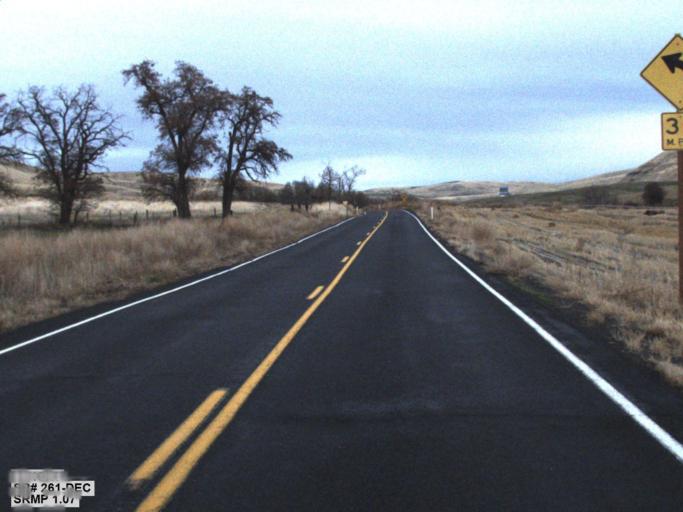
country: US
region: Washington
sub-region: Columbia County
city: Dayton
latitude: 46.5099
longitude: -117.9898
